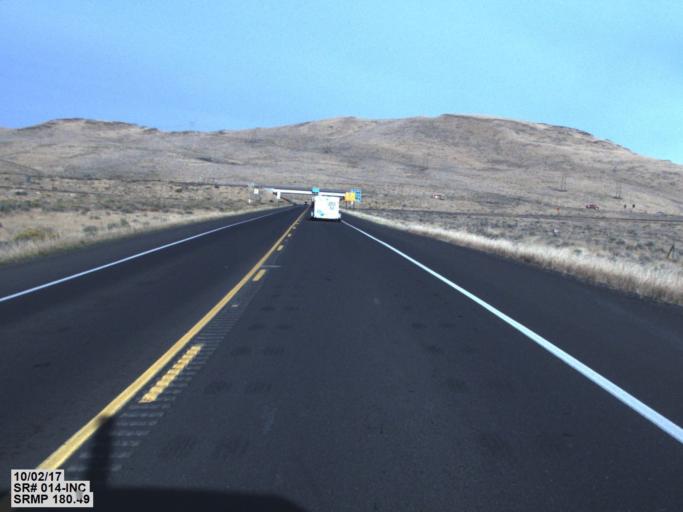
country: US
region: Oregon
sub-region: Umatilla County
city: Umatilla
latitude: 45.9442
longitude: -119.3405
